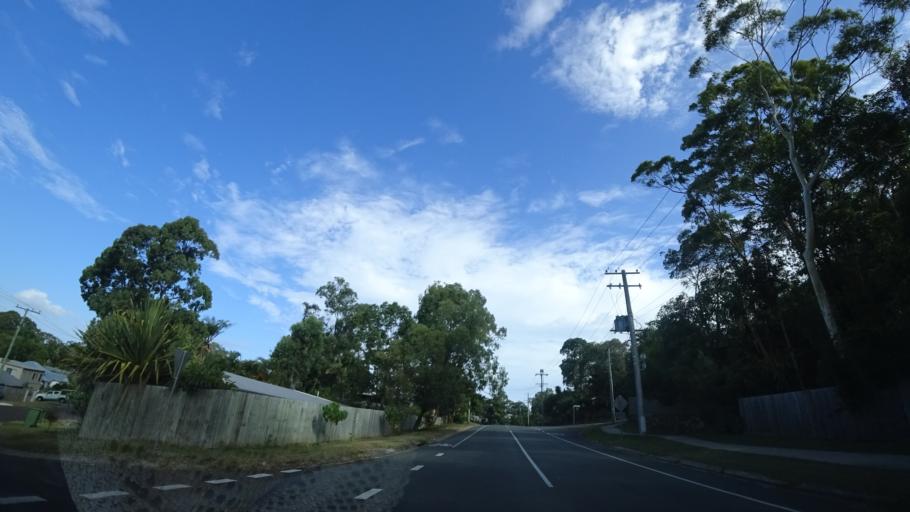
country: AU
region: Queensland
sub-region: Sunshine Coast
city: Coolum Beach
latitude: -26.5570
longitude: 153.0877
